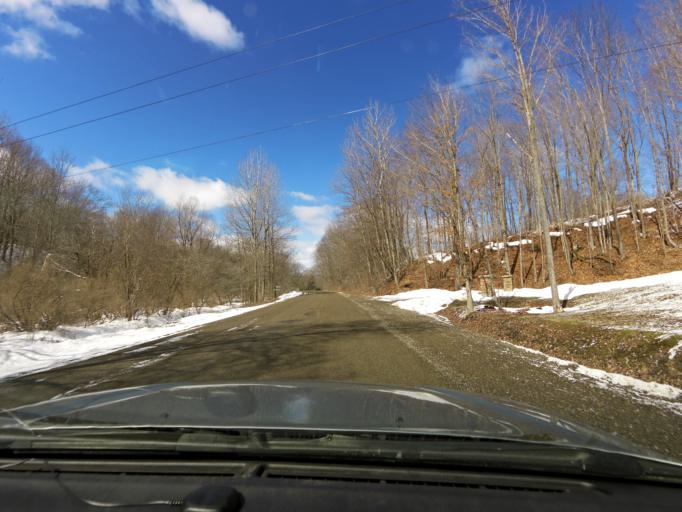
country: US
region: New York
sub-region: Cattaraugus County
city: Franklinville
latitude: 42.3429
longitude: -78.4219
